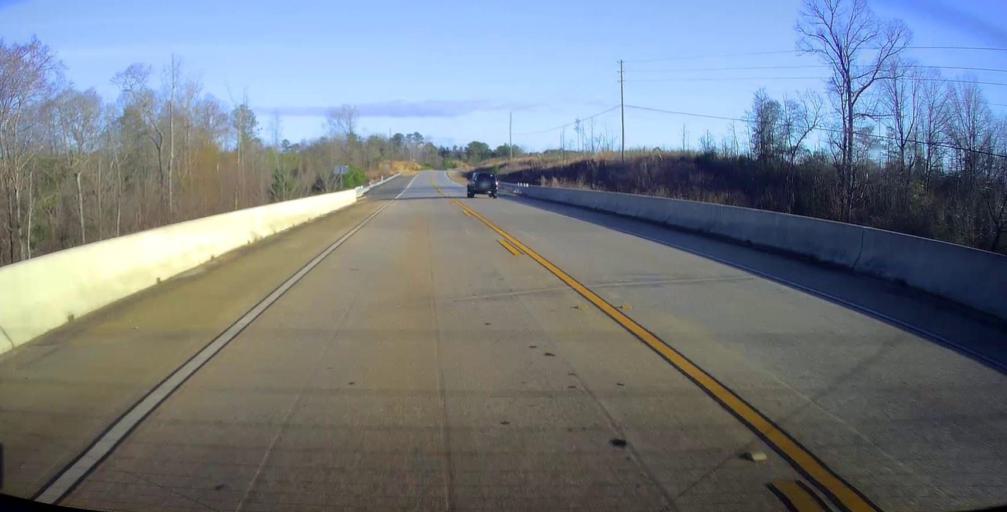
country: US
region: Alabama
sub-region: Chambers County
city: Valley
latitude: 32.8368
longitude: -85.1159
